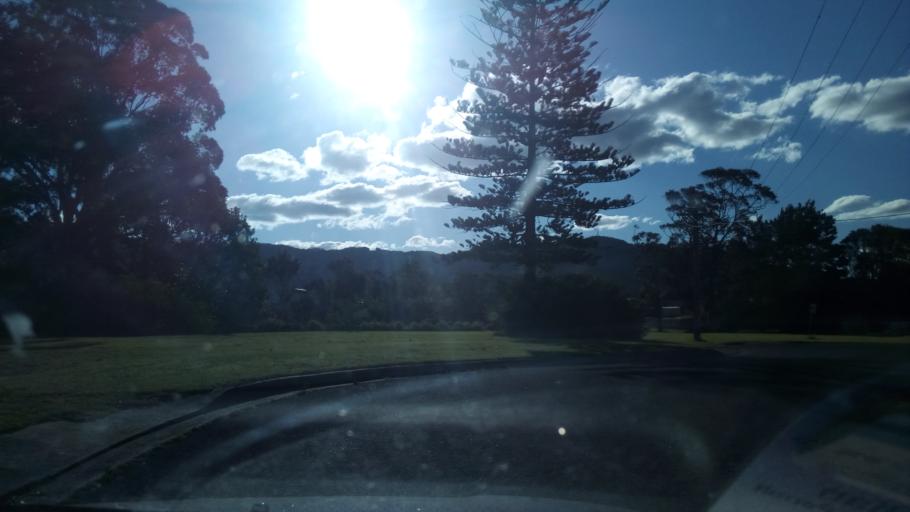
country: AU
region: New South Wales
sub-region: Wollongong
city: Fairy Meadow
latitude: -34.3951
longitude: 150.8906
